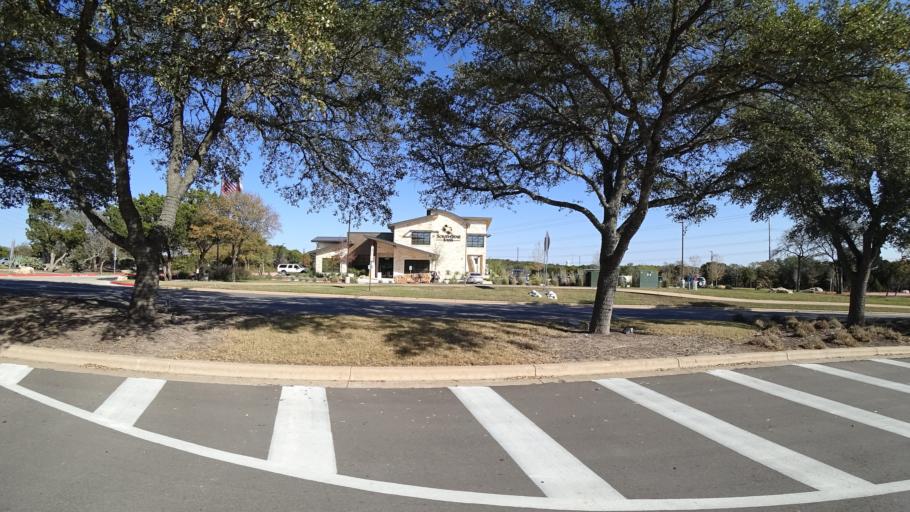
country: US
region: Texas
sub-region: Travis County
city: Hudson Bend
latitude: 30.3940
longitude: -97.8667
